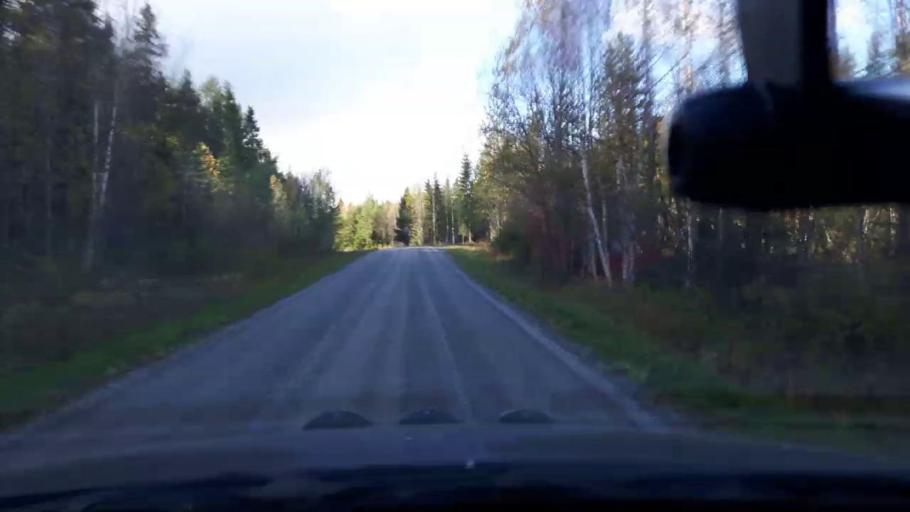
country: SE
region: Jaemtland
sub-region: Bergs Kommun
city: Hoverberg
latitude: 63.0262
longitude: 14.2829
